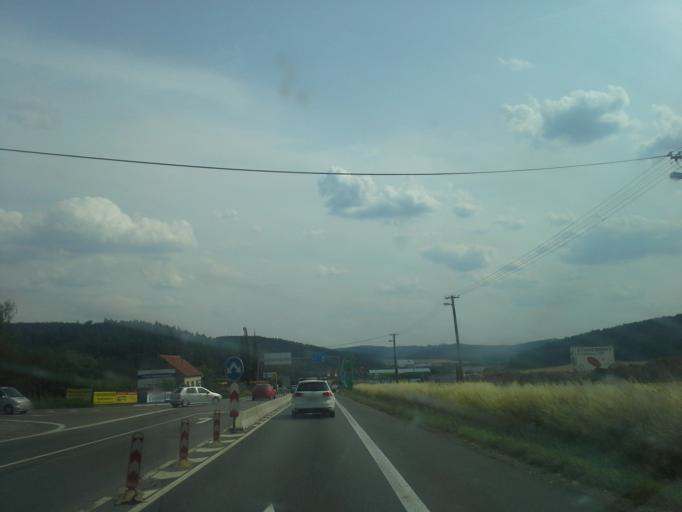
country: CZ
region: South Moravian
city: Lipuvka
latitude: 49.3363
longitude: 16.5526
